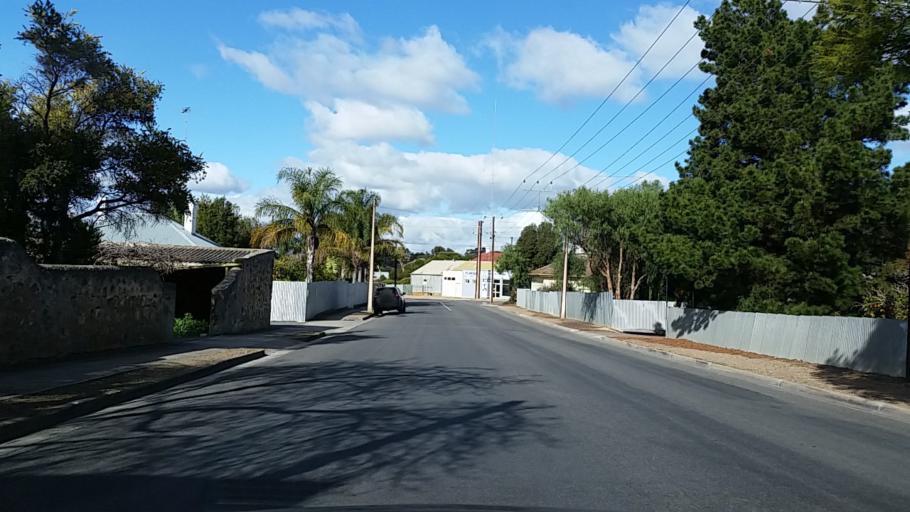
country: AU
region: South Australia
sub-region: Murray Bridge
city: Murray Bridge
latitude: -35.1209
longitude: 139.2770
